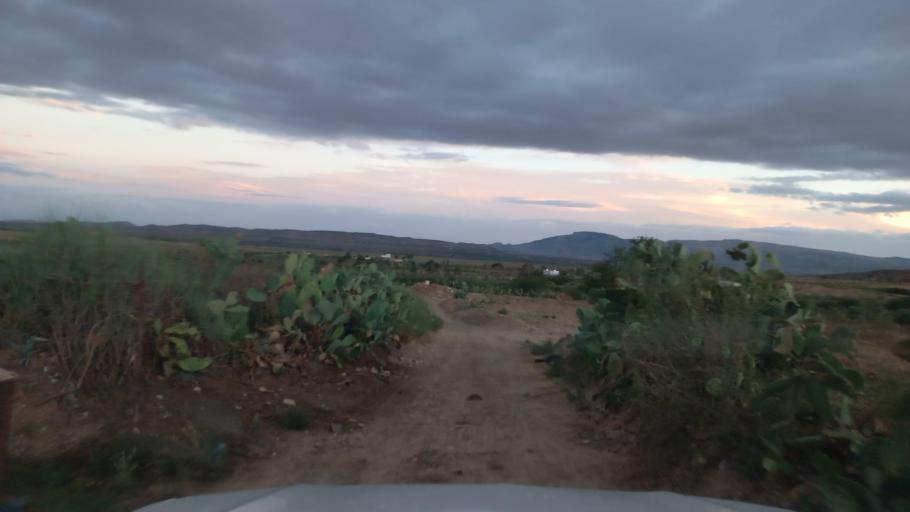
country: TN
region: Al Qasrayn
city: Kasserine
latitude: 35.2559
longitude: 8.9357
